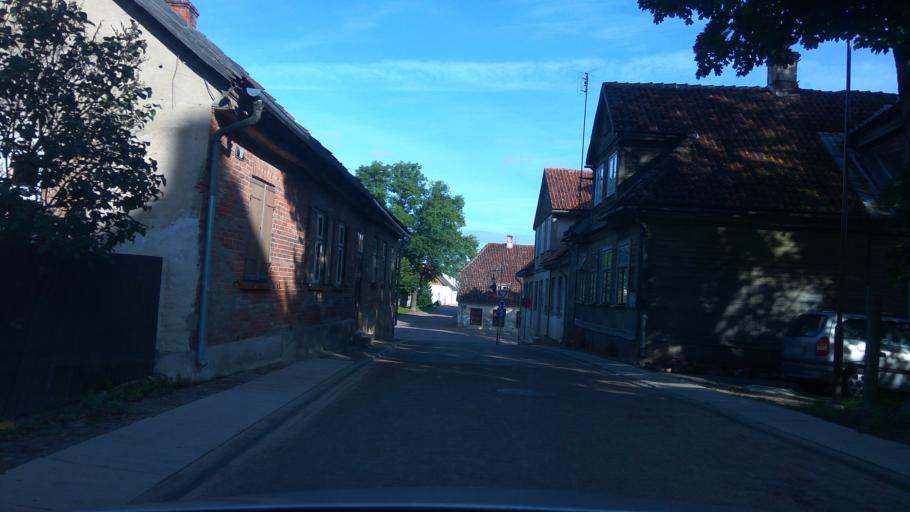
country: LV
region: Kuldigas Rajons
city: Kuldiga
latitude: 56.9711
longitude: 21.9721
